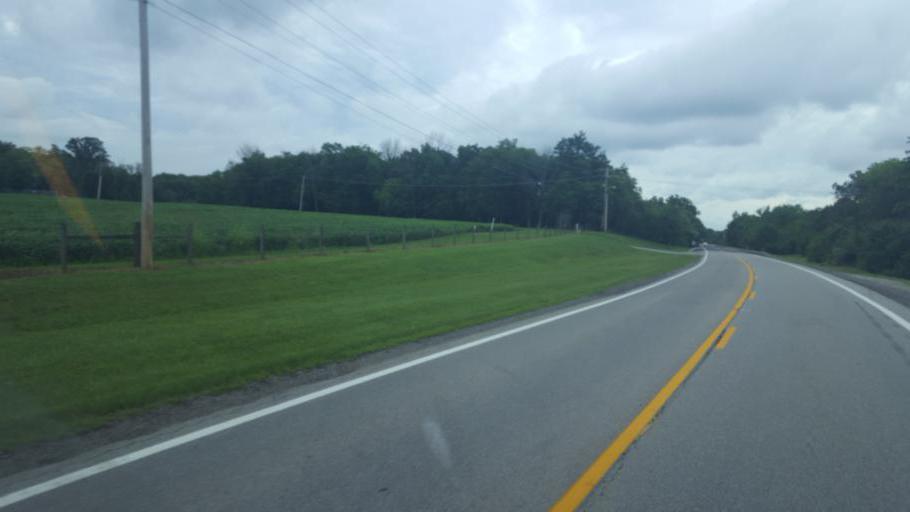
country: US
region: Ohio
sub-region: Pickaway County
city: Commercial Point
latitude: 39.7718
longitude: -83.0095
